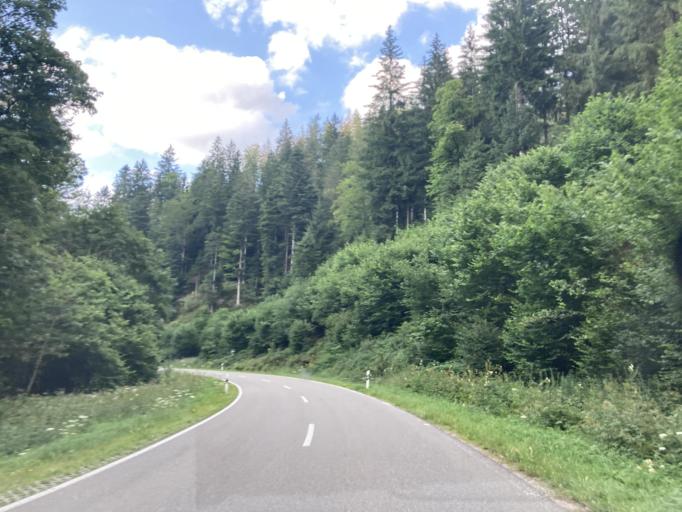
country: DE
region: Baden-Wuerttemberg
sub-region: Freiburg Region
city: Schonach im Schwarzwald
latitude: 48.1618
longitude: 8.1592
